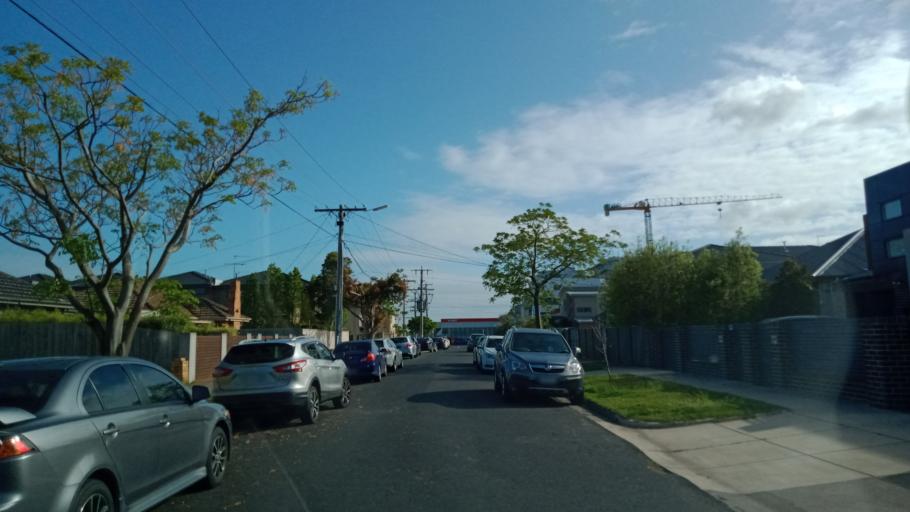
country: AU
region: Victoria
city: McKinnon
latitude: -37.9215
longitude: 145.0528
